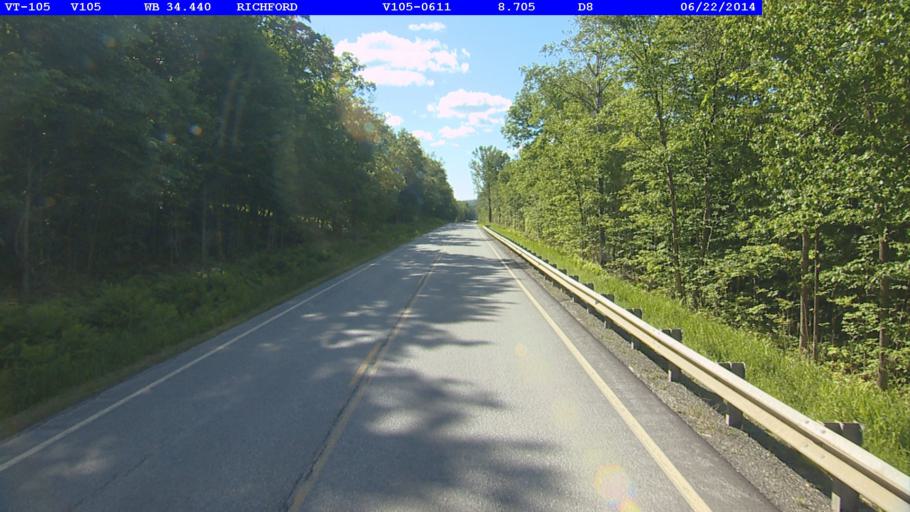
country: US
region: Vermont
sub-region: Franklin County
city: Richford
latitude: 44.9896
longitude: -72.5586
